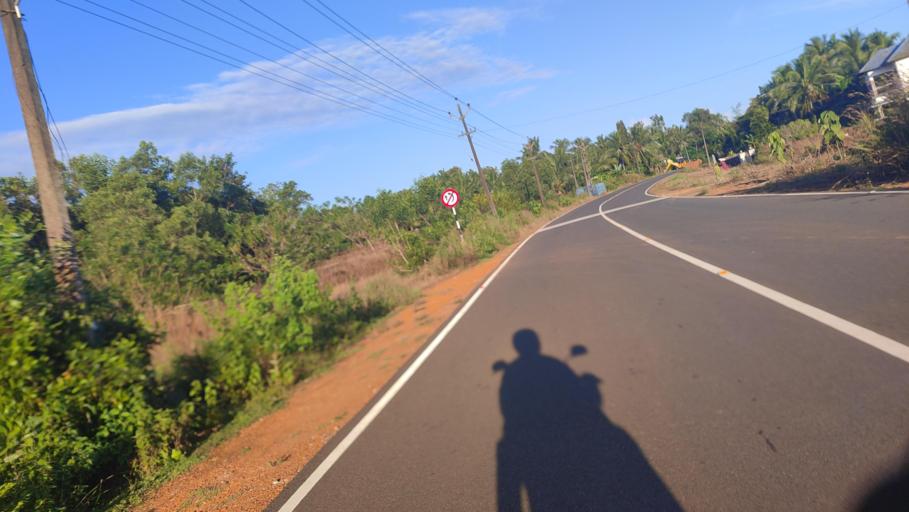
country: IN
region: Kerala
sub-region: Kasaragod District
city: Kasaragod
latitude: 12.4671
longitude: 75.0801
